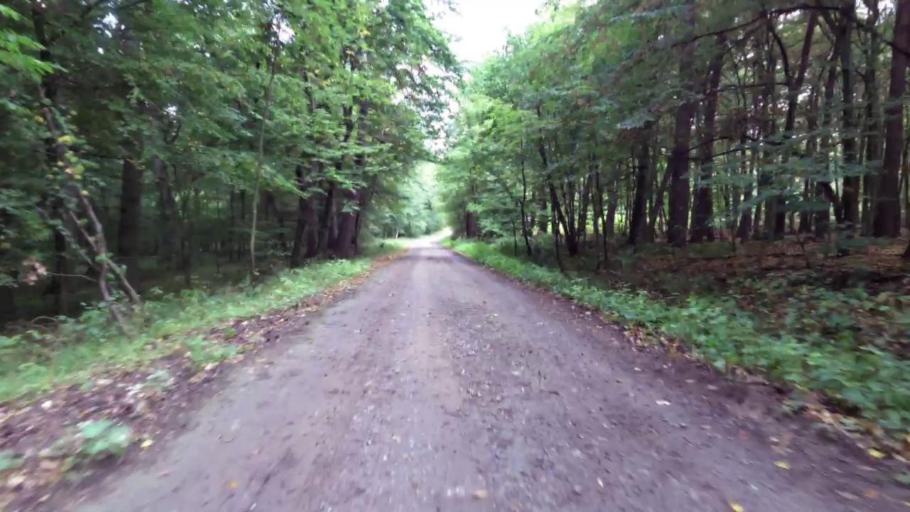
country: PL
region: West Pomeranian Voivodeship
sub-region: Powiat mysliborski
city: Debno
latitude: 52.8576
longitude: 14.6995
